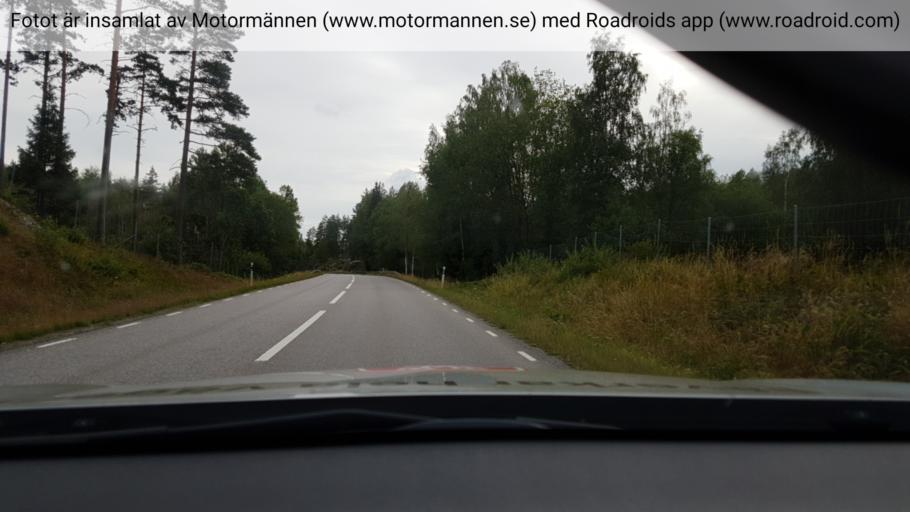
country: SE
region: Vaestra Goetaland
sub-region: Bengtsfors Kommun
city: Billingsfors
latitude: 58.9703
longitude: 12.2375
